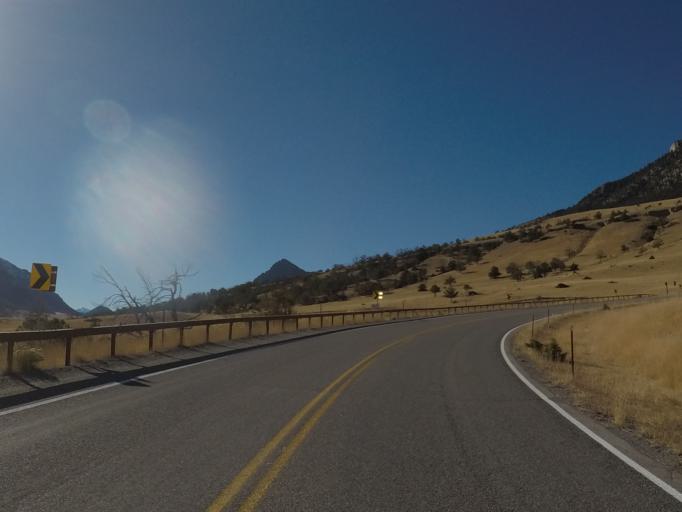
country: US
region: Wyoming
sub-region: Park County
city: Cody
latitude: 44.7695
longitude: -109.4305
